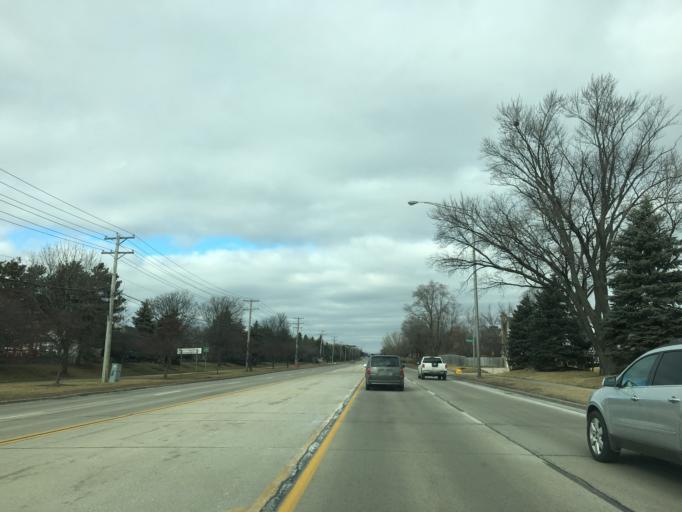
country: US
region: Illinois
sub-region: Cook County
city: Hoffman Estates
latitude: 42.0303
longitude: -88.0455
